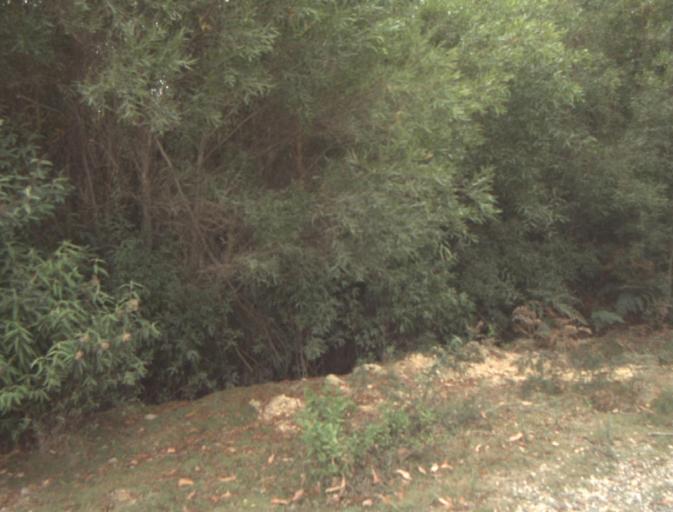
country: AU
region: Tasmania
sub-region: Launceston
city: Mayfield
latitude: -41.1581
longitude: 147.1713
